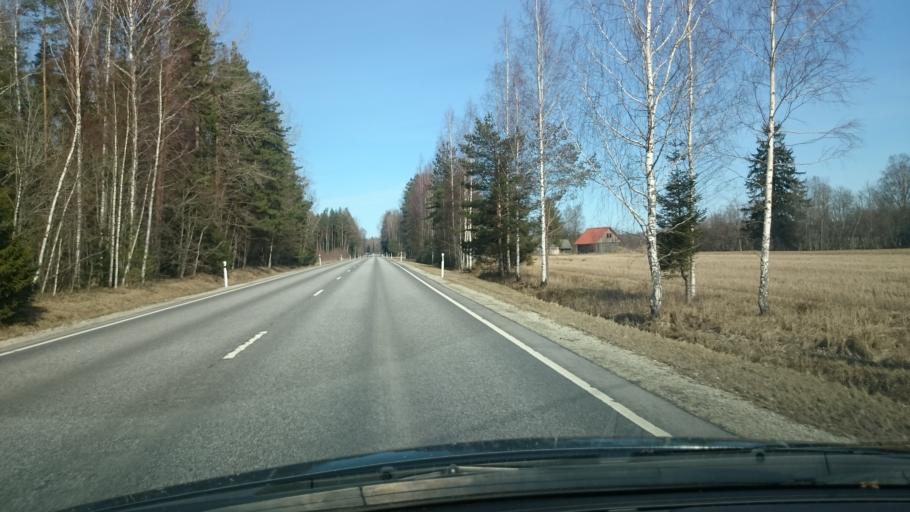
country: EE
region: Jaervamaa
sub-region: Tueri vald
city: Sarevere
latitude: 58.7082
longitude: 25.2665
